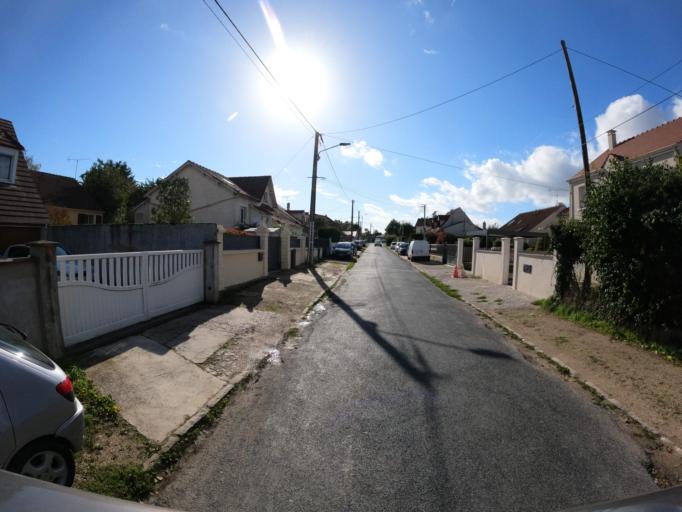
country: FR
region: Ile-de-France
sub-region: Departement de Seine-et-Marne
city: Montry
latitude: 48.8867
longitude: 2.8347
